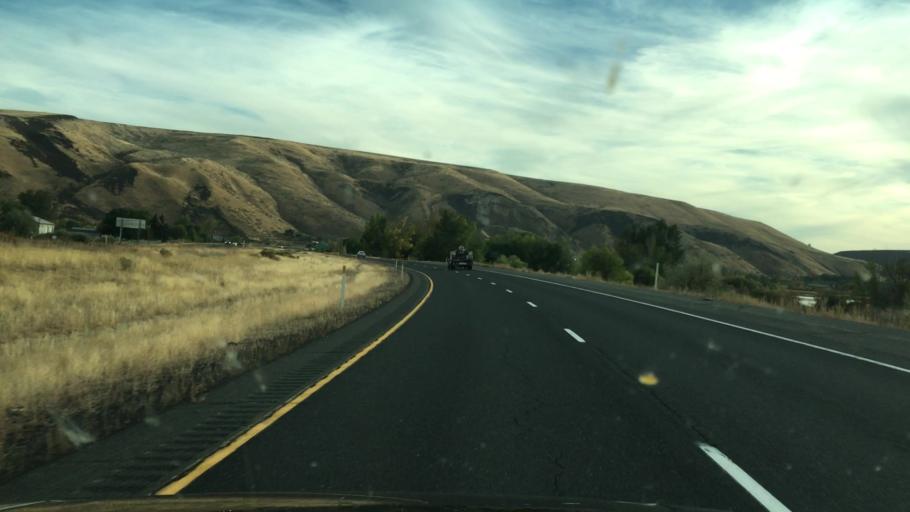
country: US
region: Washington
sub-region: Yakima County
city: Selah
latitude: 46.6593
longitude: -120.4966
